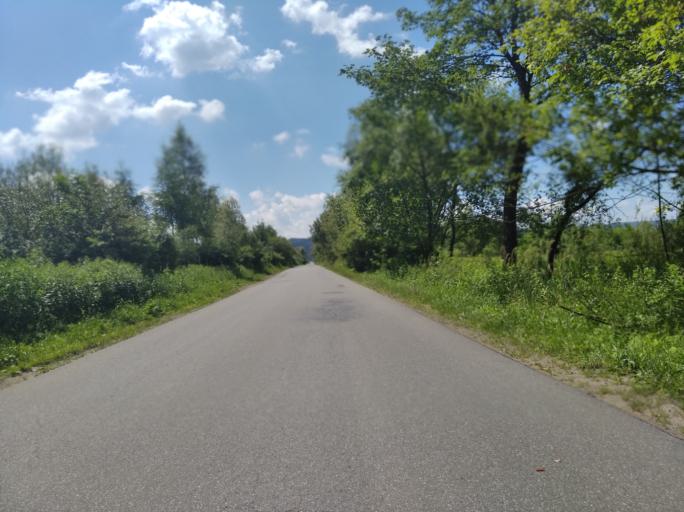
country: PL
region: Subcarpathian Voivodeship
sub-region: Powiat brzozowski
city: Dydnia
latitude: 49.7114
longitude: 22.2101
